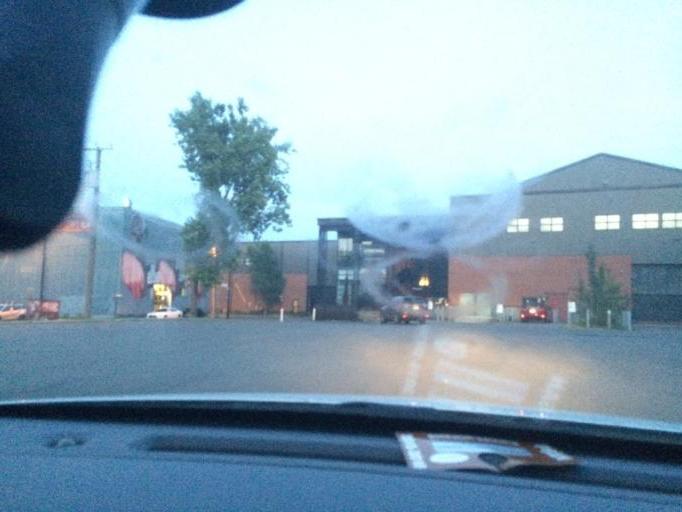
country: CA
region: Quebec
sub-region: Montreal
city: Montreal
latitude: 45.4859
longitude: -73.5701
